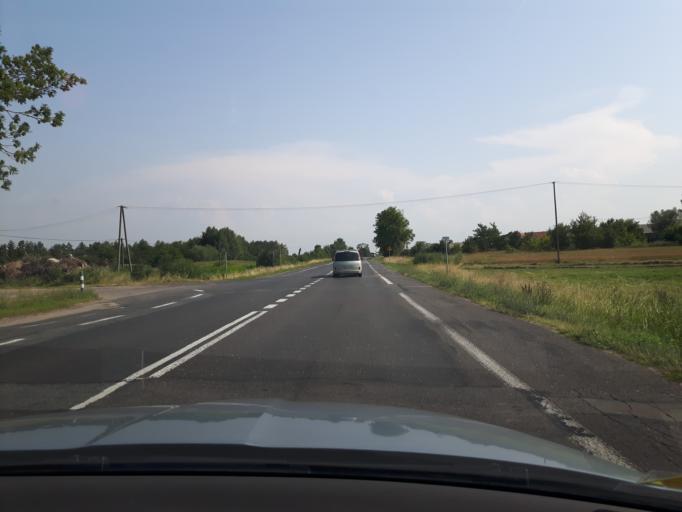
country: PL
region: Masovian Voivodeship
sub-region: Powiat plonski
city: Plonsk
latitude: 52.6780
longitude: 20.3680
